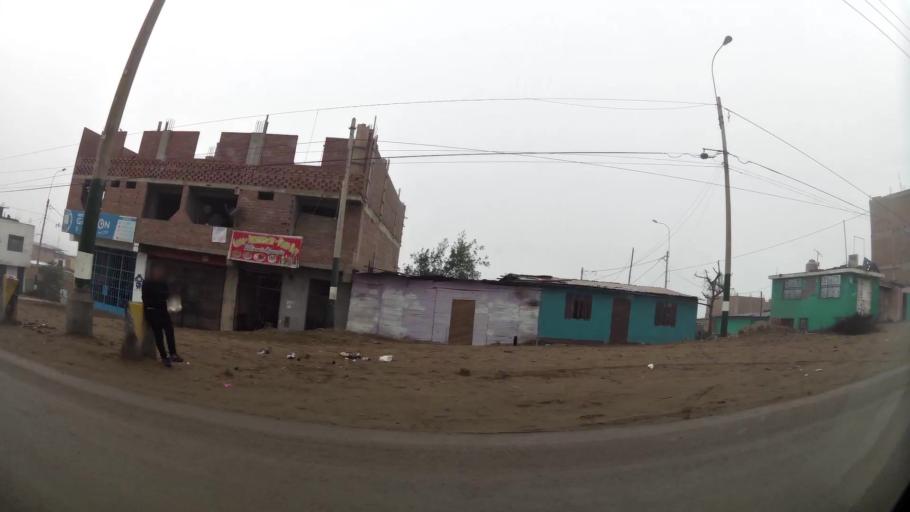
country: PE
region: Lima
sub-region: Lima
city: Santa Rosa
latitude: -11.8314
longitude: -77.1490
